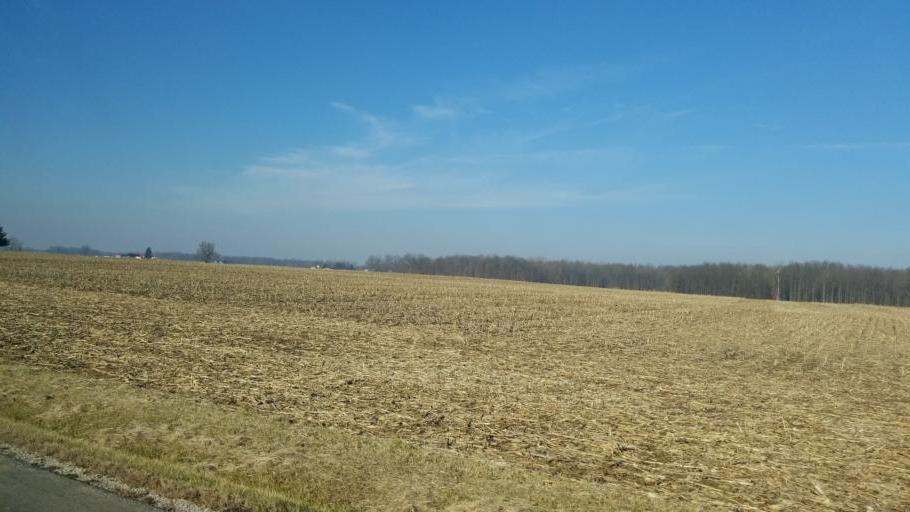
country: US
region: Ohio
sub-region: Crawford County
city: Bucyrus
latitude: 40.9067
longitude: -83.0441
